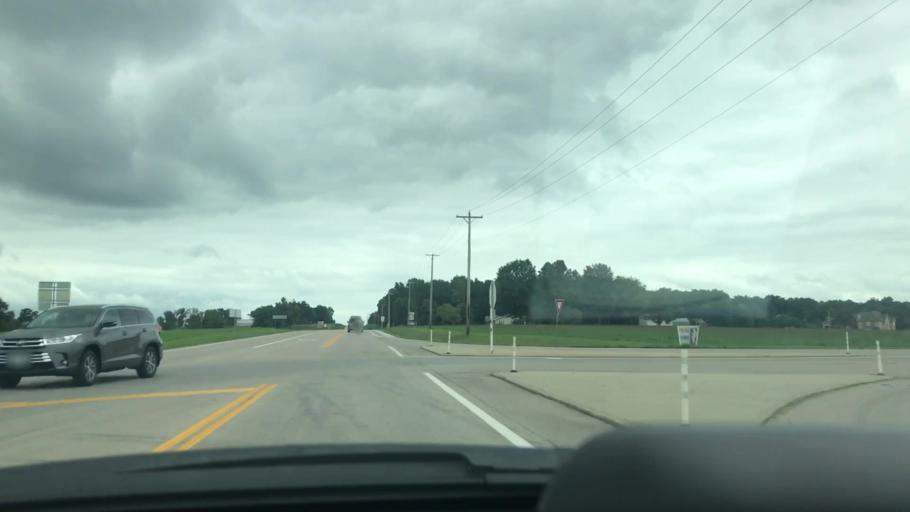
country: US
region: Missouri
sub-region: Dallas County
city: Buffalo
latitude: 37.6675
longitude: -93.1033
